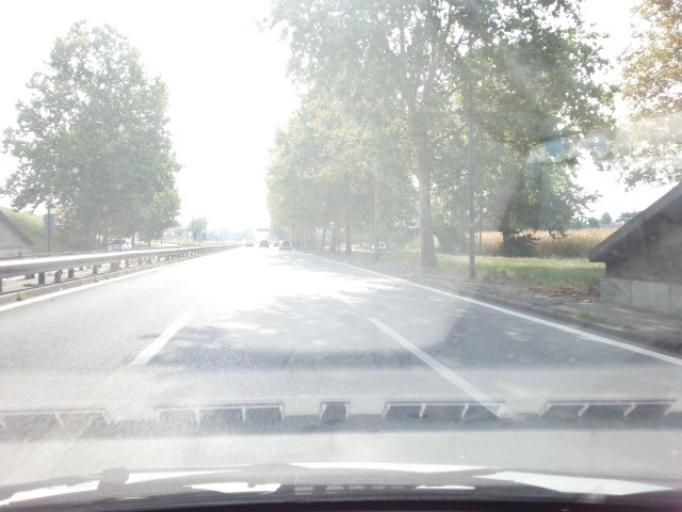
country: IT
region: Piedmont
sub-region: Provincia di Torino
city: Savonera
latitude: 45.0997
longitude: 7.6169
